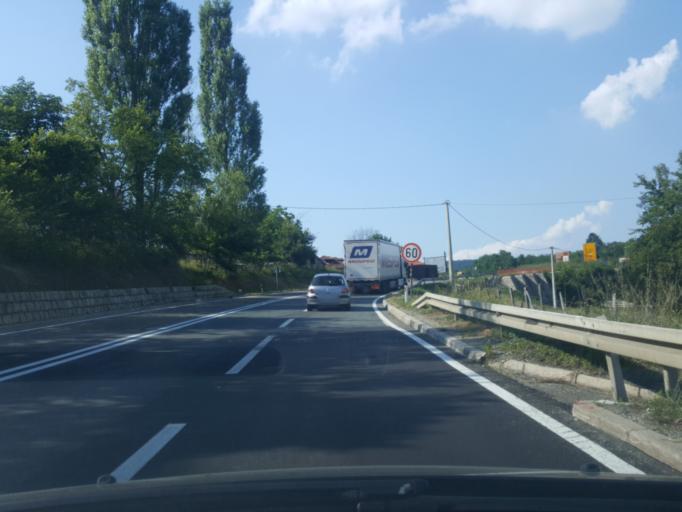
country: RS
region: Central Serbia
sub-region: Moravicki Okrug
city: Gornji Milanovac
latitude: 44.1189
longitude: 20.4827
